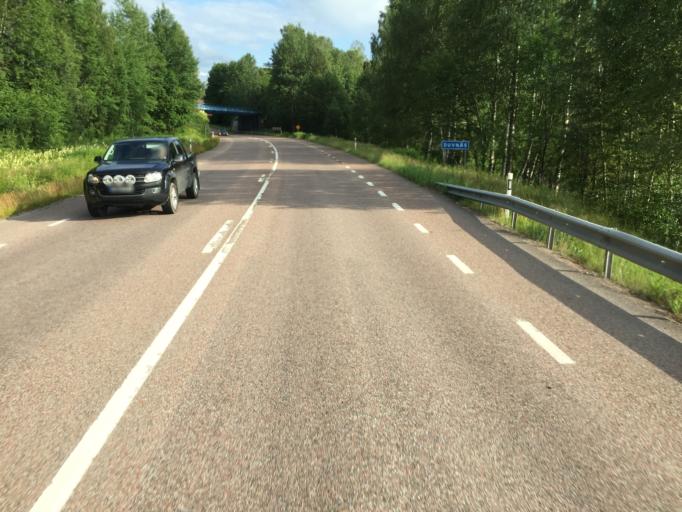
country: SE
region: Dalarna
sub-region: Gagnefs Kommun
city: Djuras
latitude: 60.5420
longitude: 15.2804
